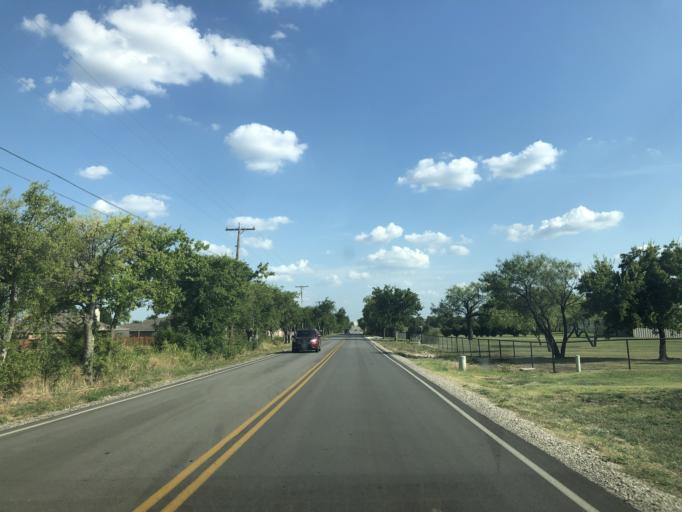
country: US
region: Texas
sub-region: Tarrant County
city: Saginaw
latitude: 32.8903
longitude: -97.3946
